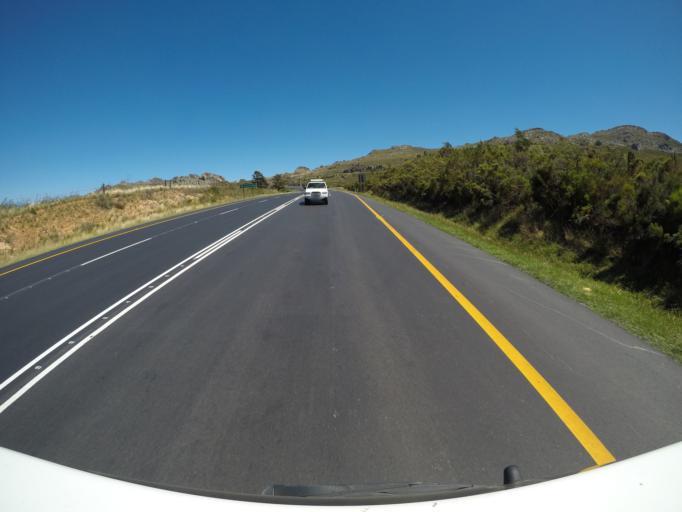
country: ZA
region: Western Cape
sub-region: Overberg District Municipality
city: Grabouw
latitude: -34.1510
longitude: 18.9360
